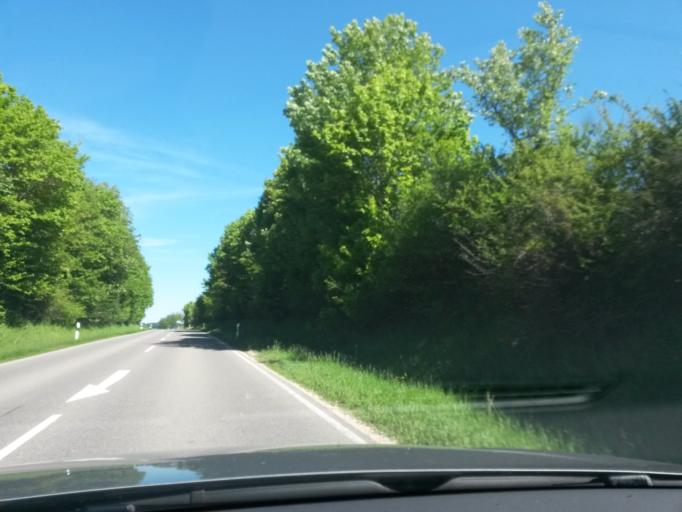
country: DE
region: Baden-Wuerttemberg
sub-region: Tuebingen Region
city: Hettingen
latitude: 48.2440
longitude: 9.2911
